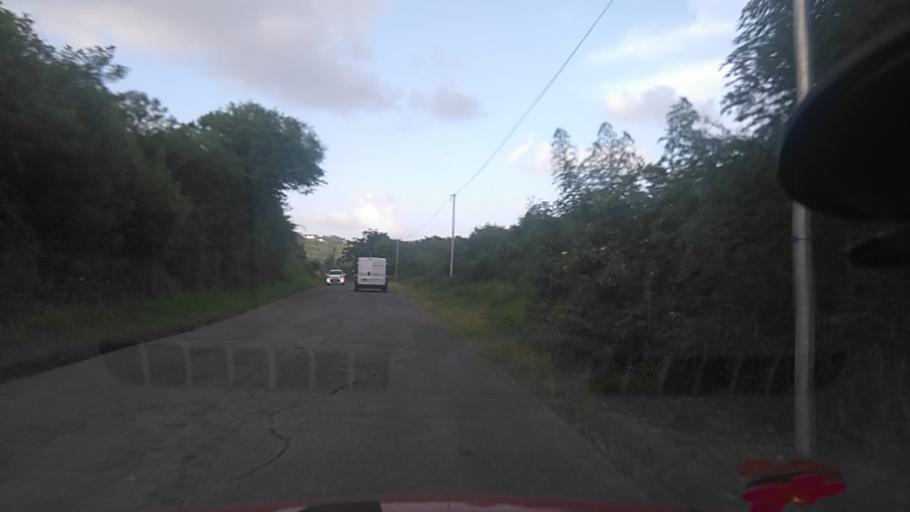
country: MQ
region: Martinique
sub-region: Martinique
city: Le Marin
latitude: 14.4673
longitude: -60.8621
